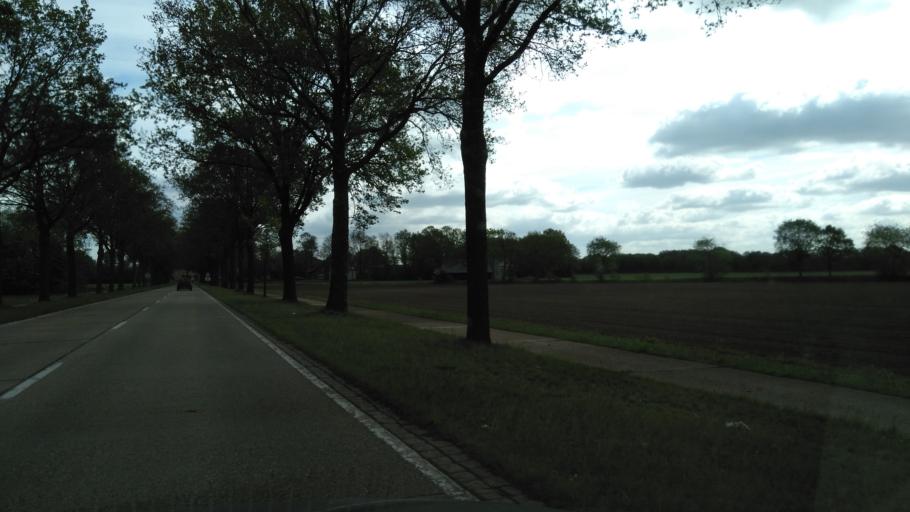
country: NL
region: North Brabant
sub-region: Gemeente Goirle
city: Goirle
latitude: 51.5112
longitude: 4.9892
